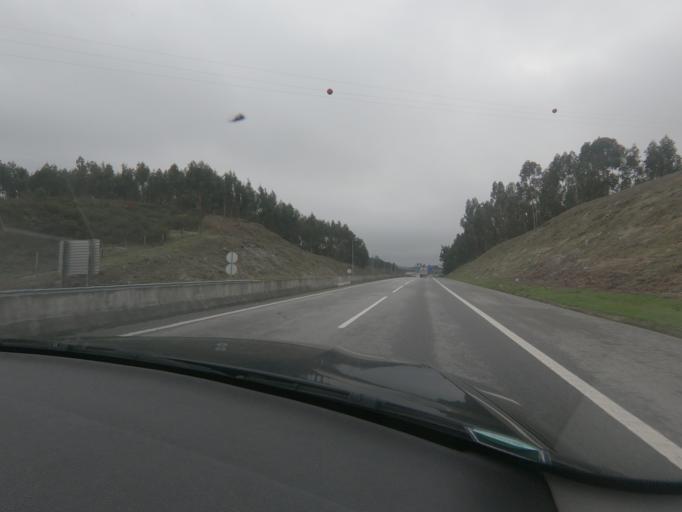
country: PT
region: Viseu
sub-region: Viseu
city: Viseu
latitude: 40.6313
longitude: -7.9595
